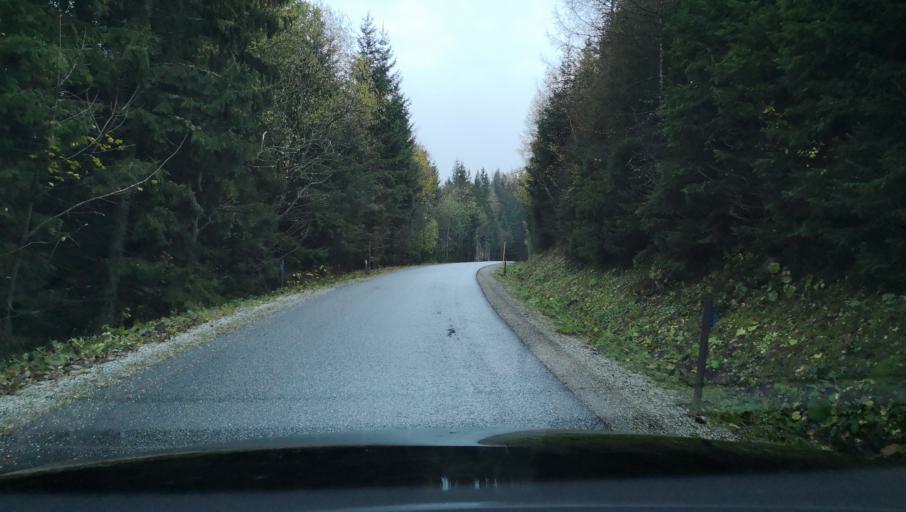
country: AT
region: Styria
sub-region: Politischer Bezirk Weiz
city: Gasen
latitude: 47.3590
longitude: 15.5845
